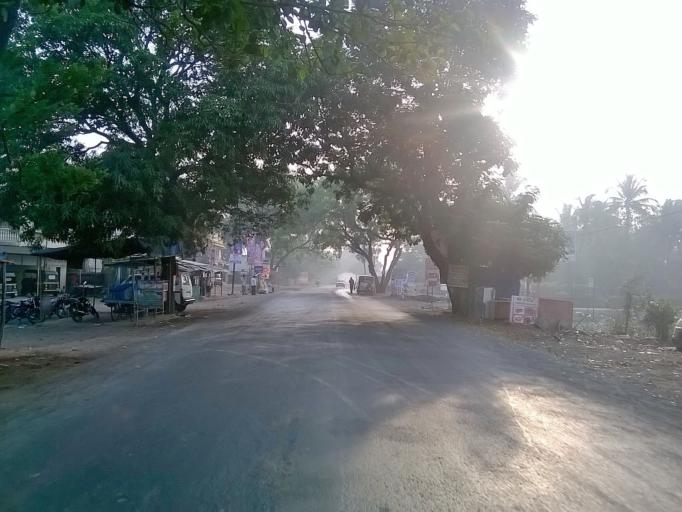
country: IN
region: Maharashtra
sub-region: Raigarh
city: Kalundri
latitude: 19.0025
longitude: 73.1415
